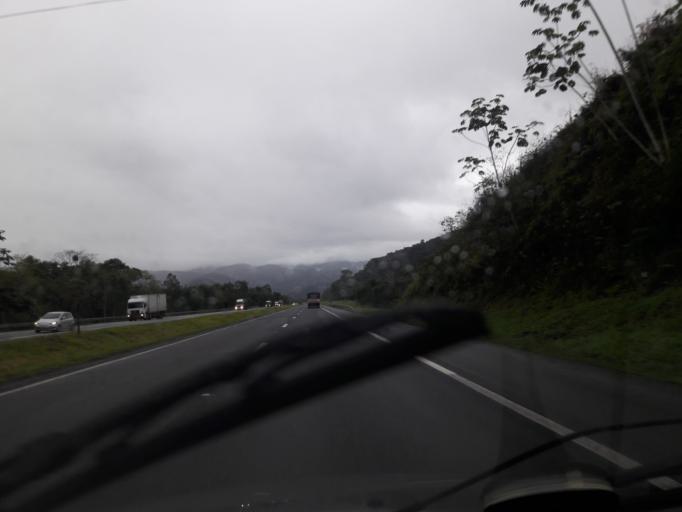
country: BR
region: Sao Paulo
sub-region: Miracatu
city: Miracatu
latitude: -24.2178
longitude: -47.3664
